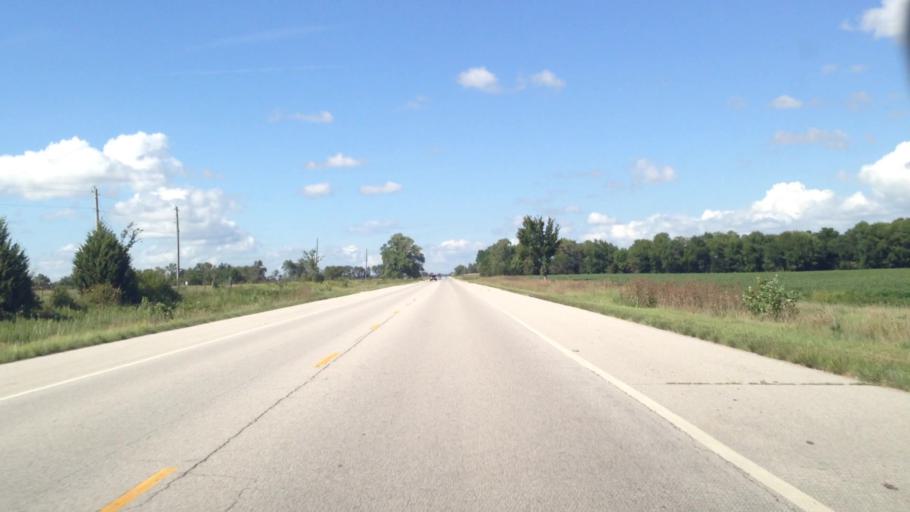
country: US
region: Kansas
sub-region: Labette County
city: Parsons
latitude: 37.4193
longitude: -95.2702
